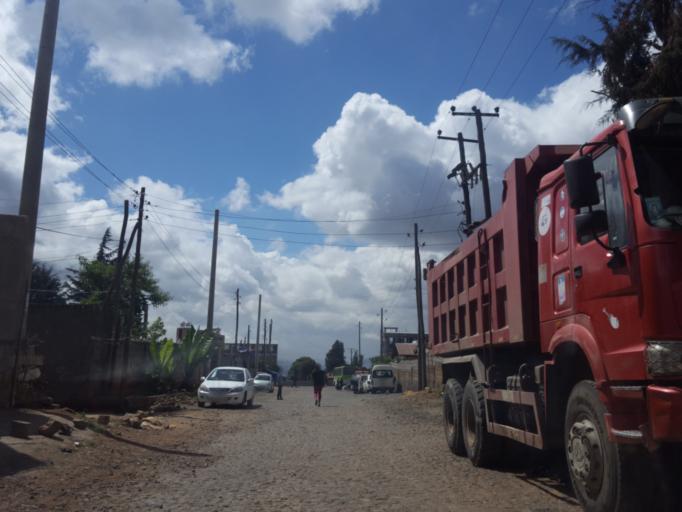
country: ET
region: Adis Abeba
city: Addis Ababa
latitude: 9.0642
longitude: 38.7319
